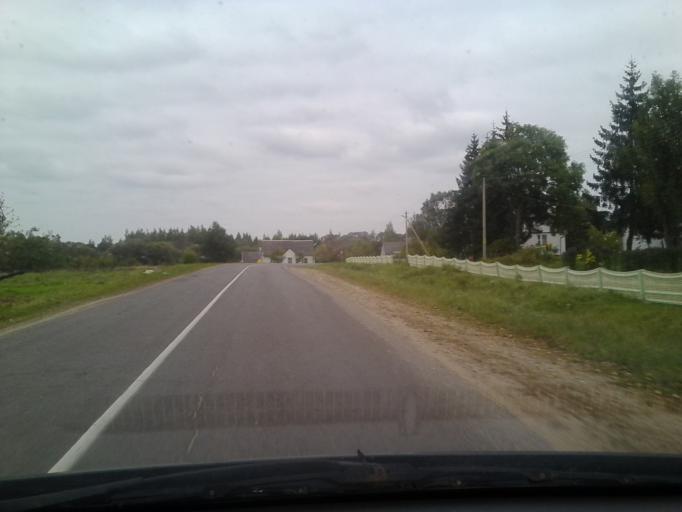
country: BY
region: Vitebsk
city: Pastavy
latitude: 55.1168
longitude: 26.9231
